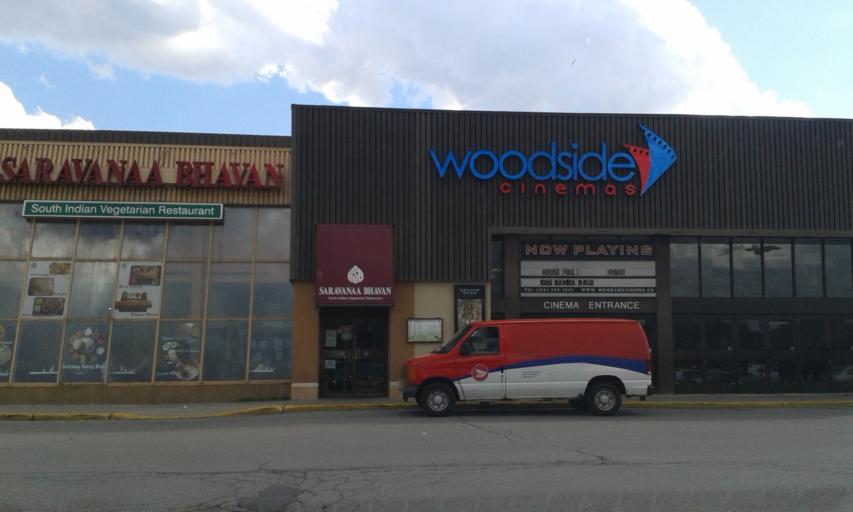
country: CA
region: Ontario
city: Scarborough
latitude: 43.8104
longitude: -79.2692
